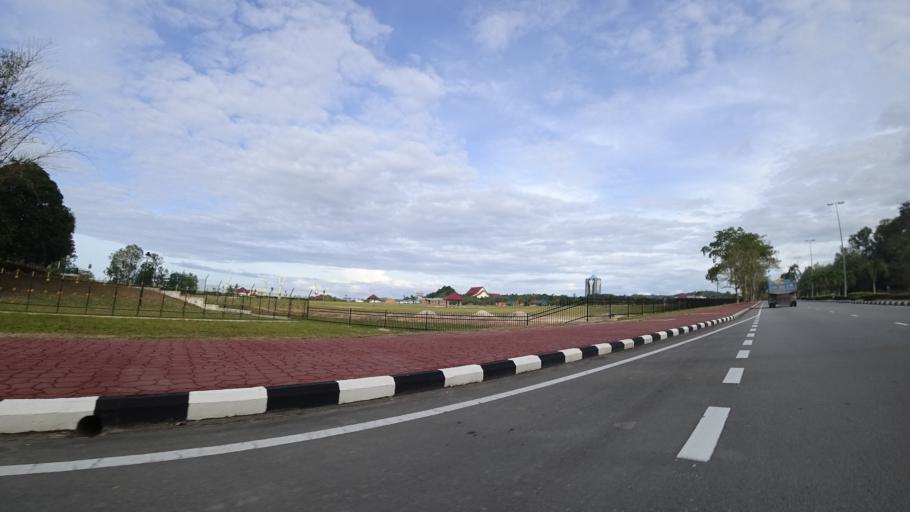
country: BN
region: Brunei and Muara
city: Bandar Seri Begawan
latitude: 4.9228
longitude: 114.9389
